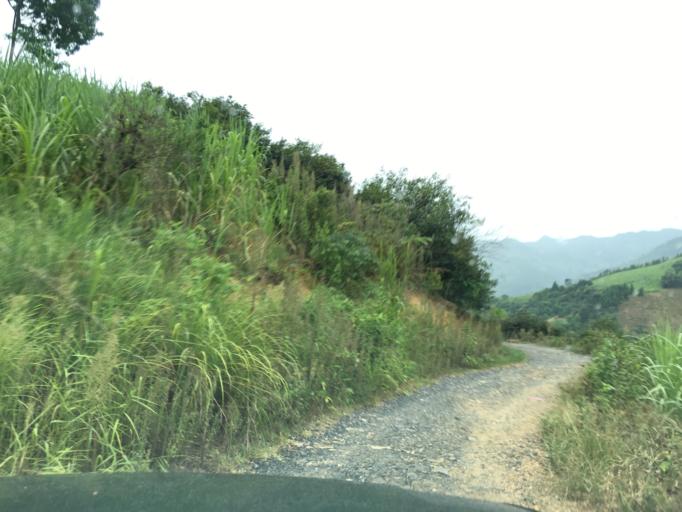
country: CN
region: Guangxi Zhuangzu Zizhiqu
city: Tongle
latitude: 25.0018
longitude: 105.9941
